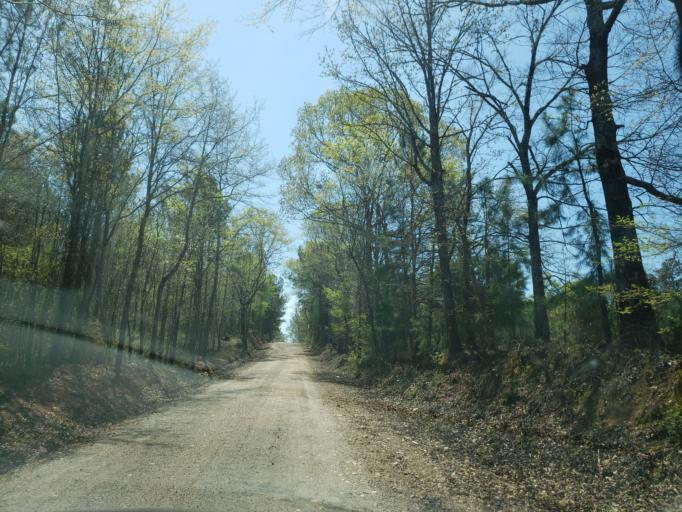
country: US
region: Alabama
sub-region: Tallapoosa County
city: Camp Hill
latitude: 32.6628
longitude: -85.6623
